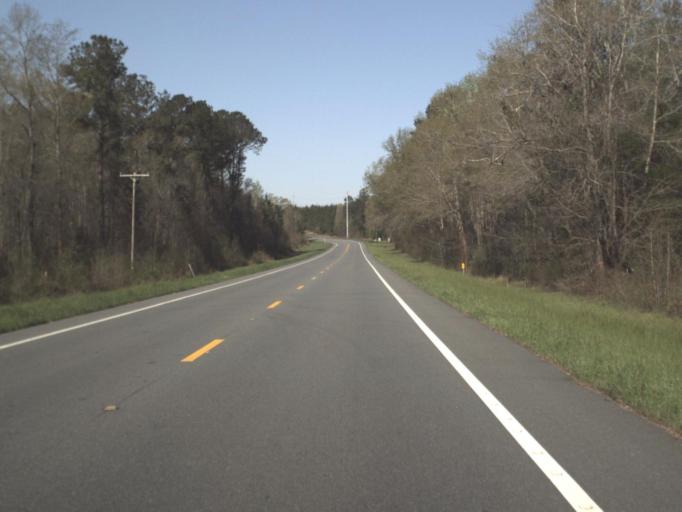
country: US
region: Alabama
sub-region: Houston County
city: Cottonwood
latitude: 30.9448
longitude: -85.2803
